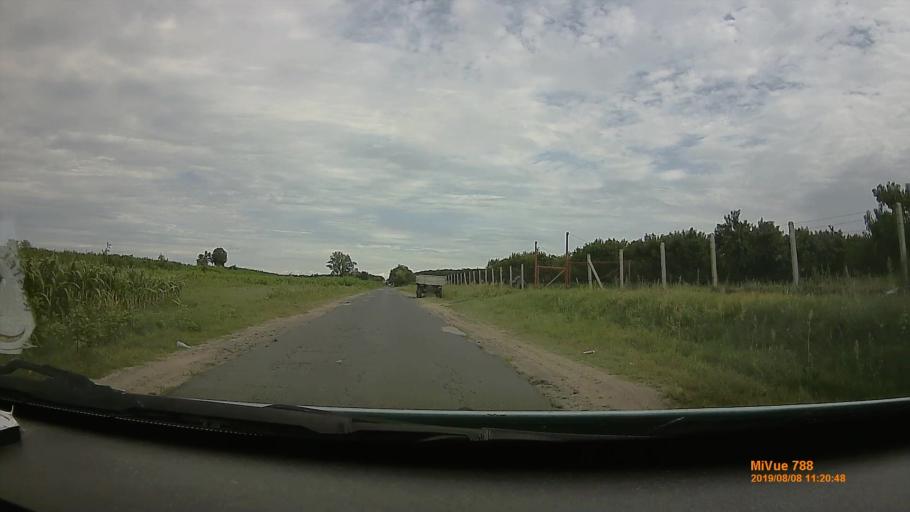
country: HU
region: Szabolcs-Szatmar-Bereg
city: Balkany
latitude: 47.7534
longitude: 21.8446
